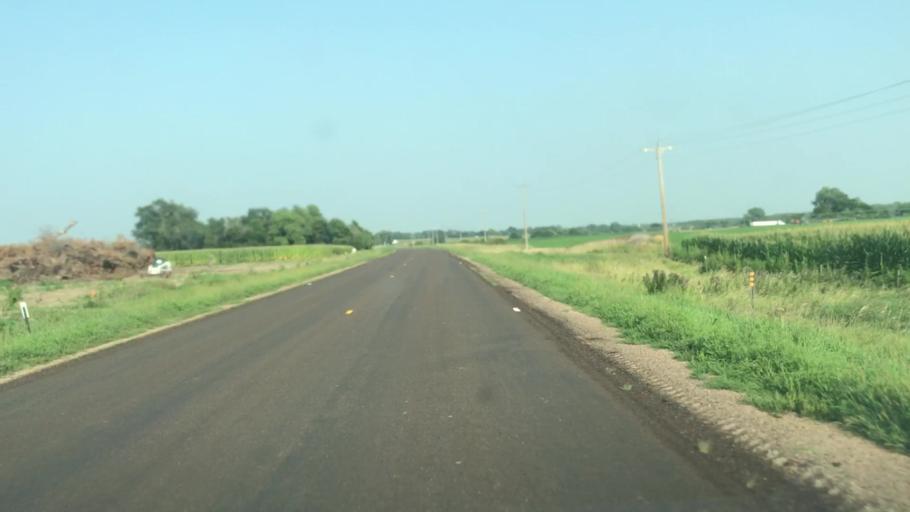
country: US
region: Nebraska
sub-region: Buffalo County
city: Ravenna
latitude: 41.0756
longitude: -98.7410
